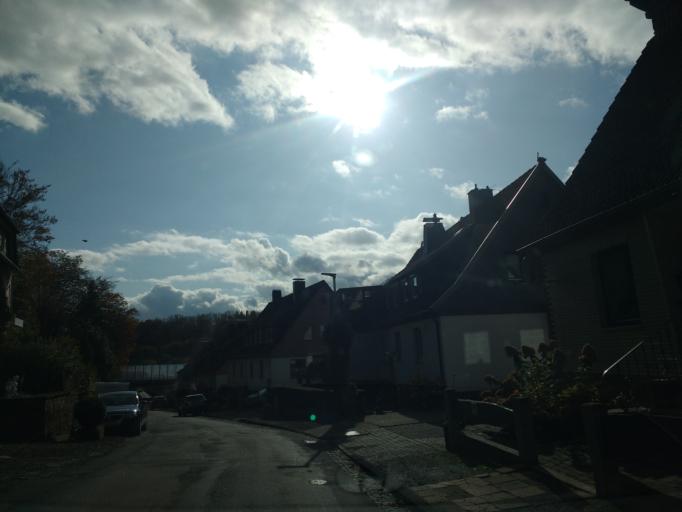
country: DE
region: Lower Saxony
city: Herzberg am Harz
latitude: 51.6317
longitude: 10.3857
